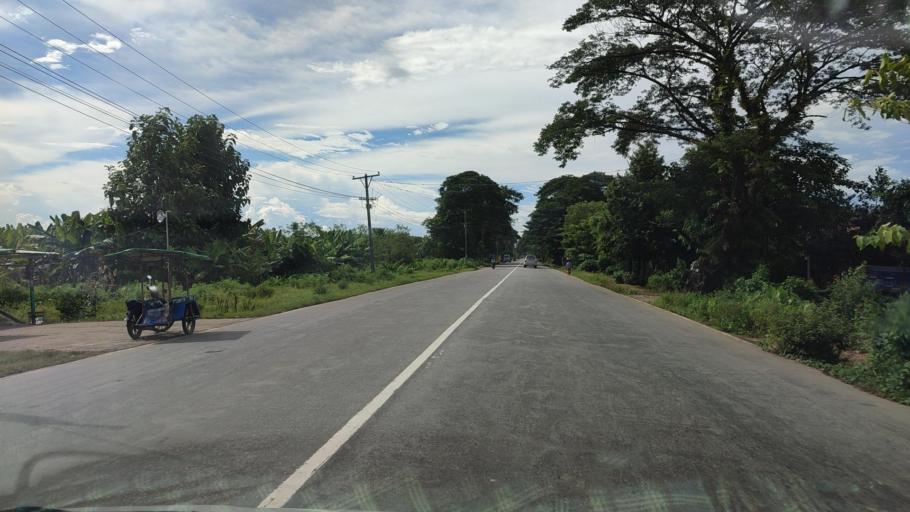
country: MM
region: Bago
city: Pyu
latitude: 18.3238
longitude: 96.4991
